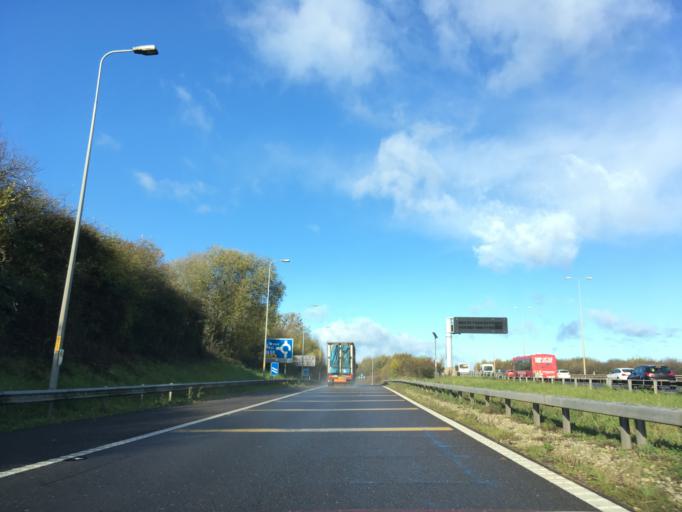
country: GB
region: England
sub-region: Worcestershire
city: Bredon
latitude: 52.0447
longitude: -2.1341
